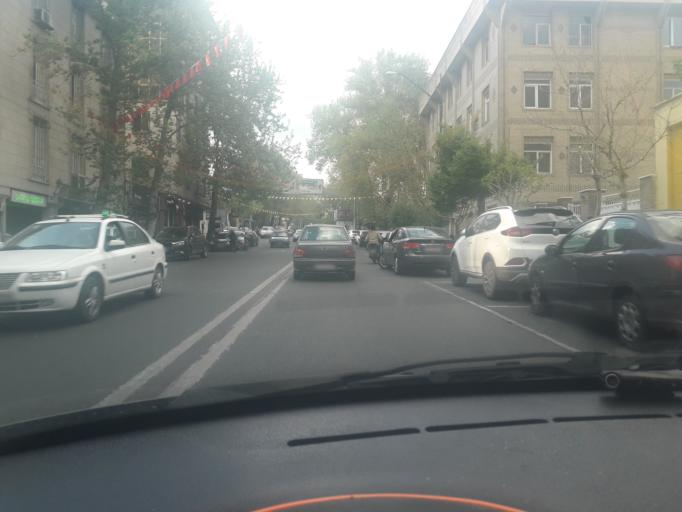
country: IR
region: Tehran
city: Tehran
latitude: 35.7433
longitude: 51.4051
